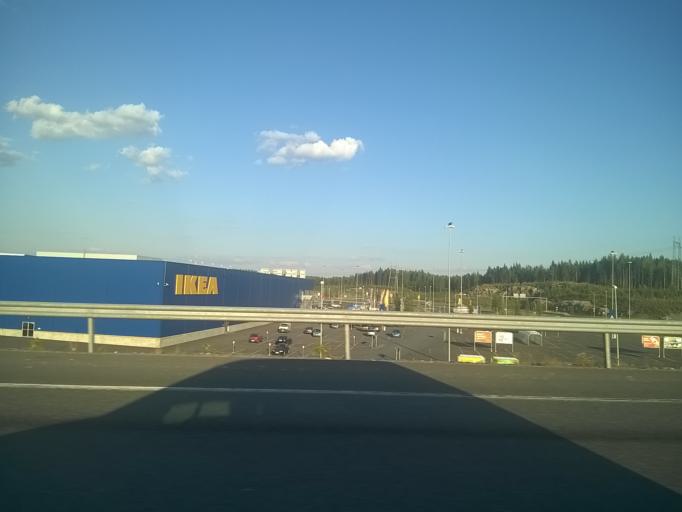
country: FI
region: Pirkanmaa
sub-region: Tampere
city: Tampere
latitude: 61.4529
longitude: 23.7677
